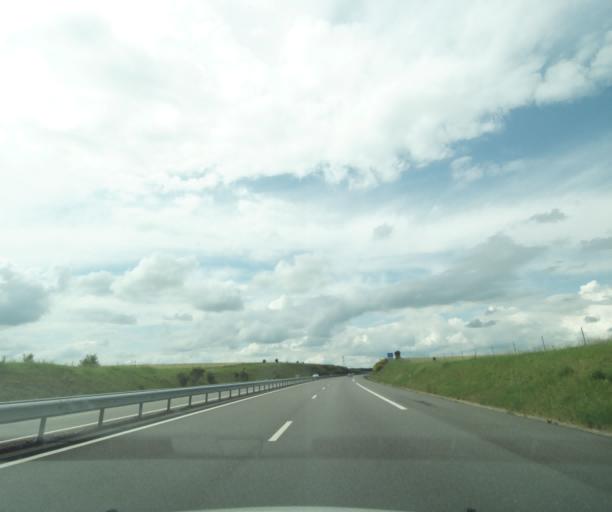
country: FR
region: Centre
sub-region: Departement du Cher
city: Trouy
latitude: 47.0122
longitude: 2.3851
